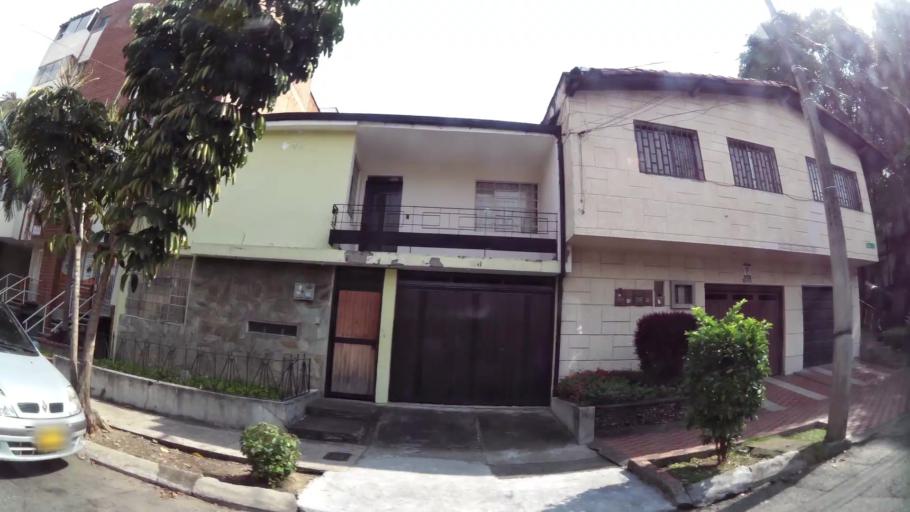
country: CO
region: Antioquia
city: Medellin
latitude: 6.2352
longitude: -75.5921
